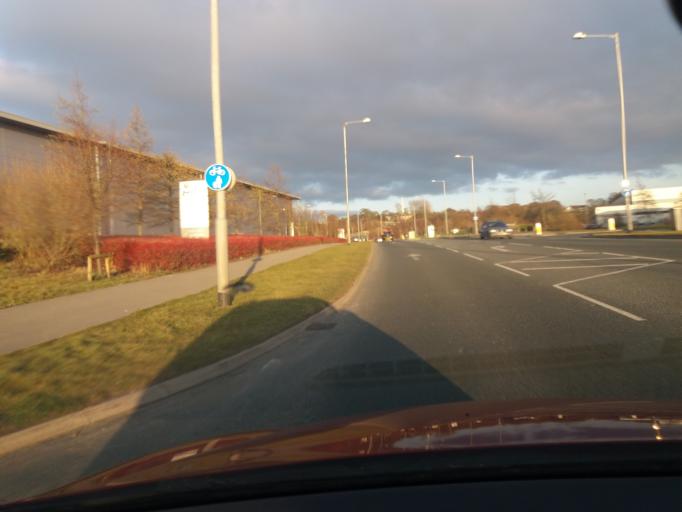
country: GB
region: England
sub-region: Lancashire
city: Euxton
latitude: 53.6734
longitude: -2.6443
